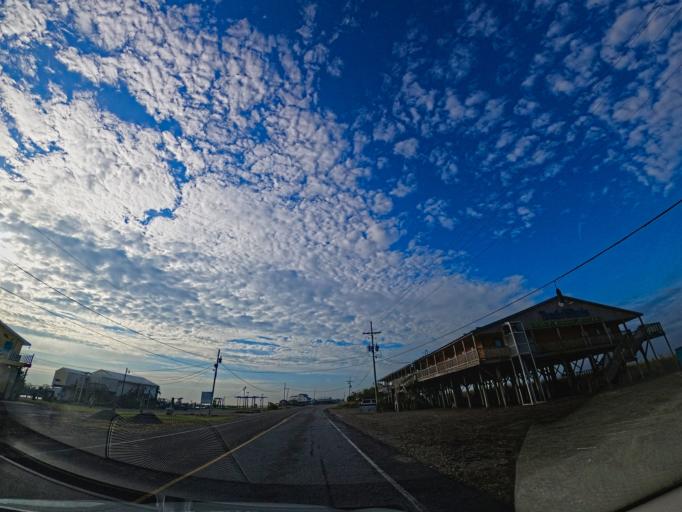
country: US
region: Louisiana
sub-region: Terrebonne Parish
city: Dulac
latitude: 29.2796
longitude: -90.6444
